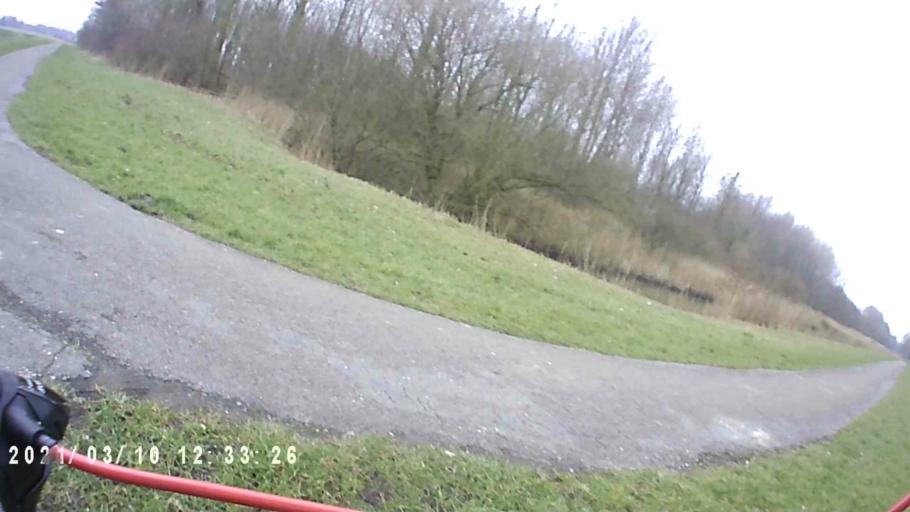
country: NL
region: Groningen
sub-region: Gemeente Bedum
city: Bedum
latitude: 53.2531
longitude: 6.6357
